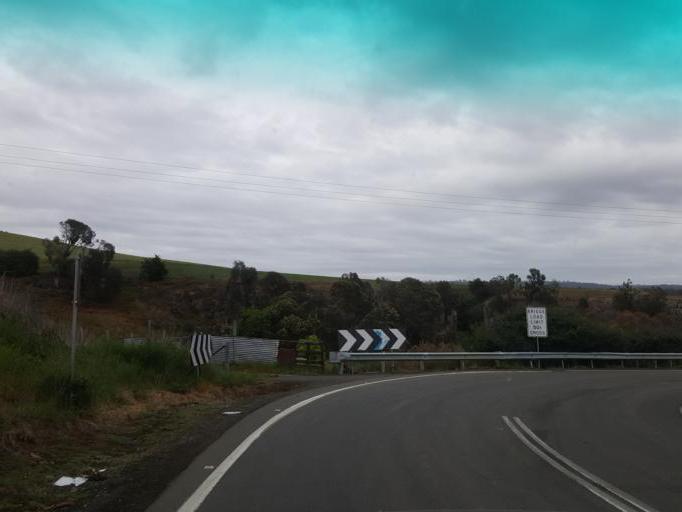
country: AU
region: Tasmania
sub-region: Northern Midlands
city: Evandale
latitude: -41.4882
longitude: 147.2329
